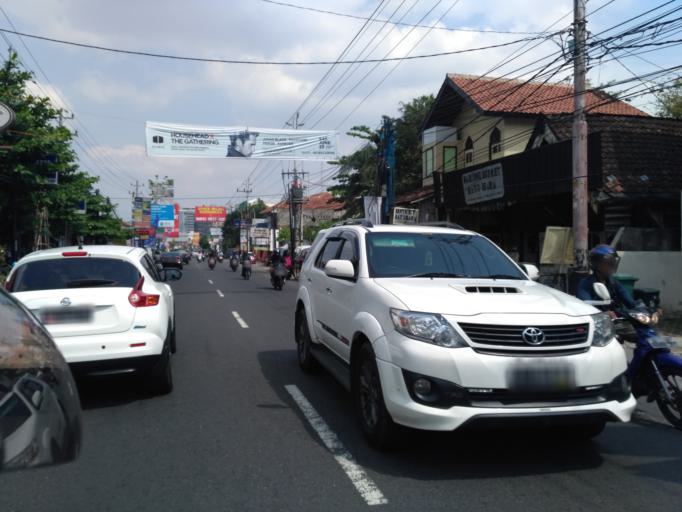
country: ID
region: Daerah Istimewa Yogyakarta
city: Melati
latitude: -7.7523
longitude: 110.3848
